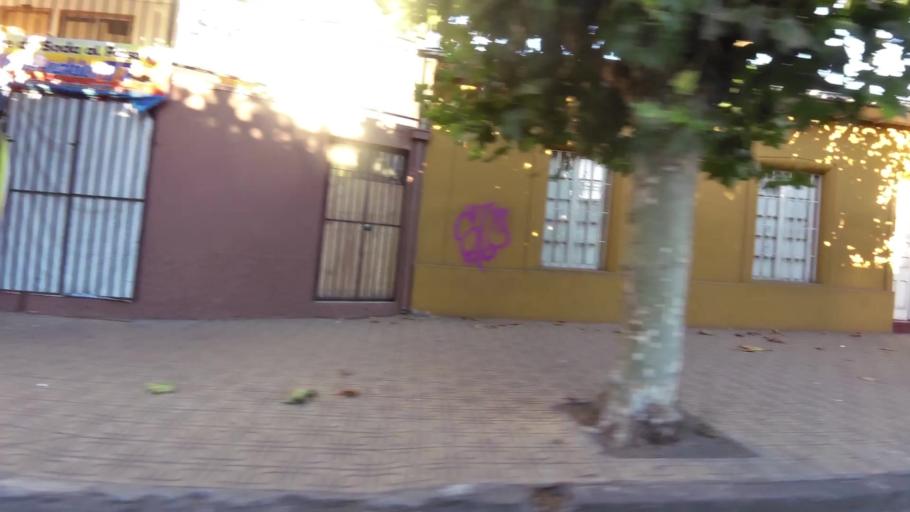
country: CL
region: Maule
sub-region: Provincia de Curico
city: Curico
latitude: -34.9855
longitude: -71.2442
